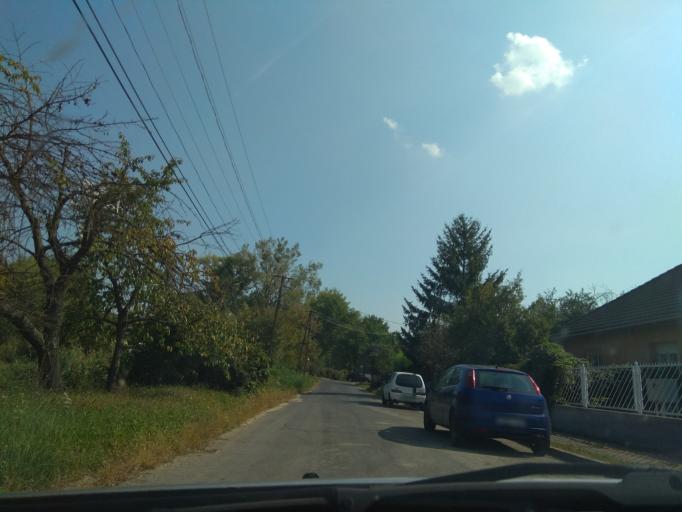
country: HU
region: Borsod-Abauj-Zemplen
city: Miskolc
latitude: 48.0733
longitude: 20.7728
